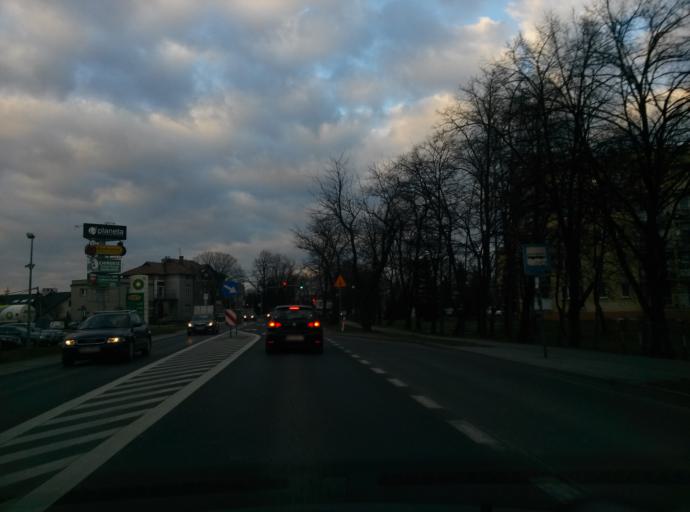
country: PL
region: Lesser Poland Voivodeship
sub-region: Powiat brzeski
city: Brzesko
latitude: 49.9626
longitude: 20.5988
